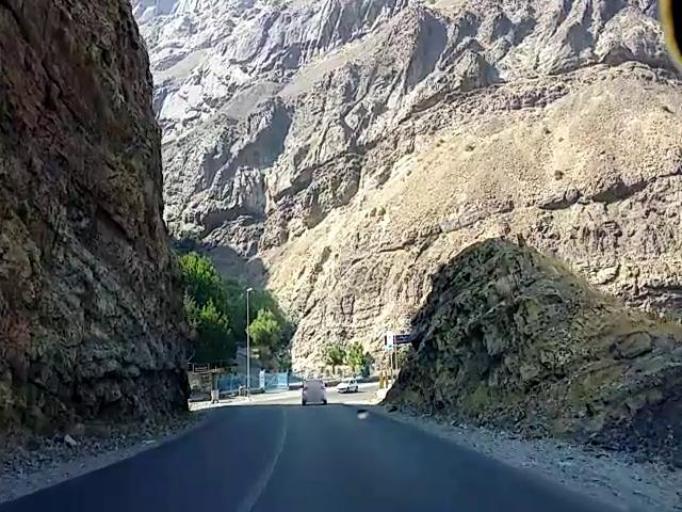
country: IR
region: Alborz
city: Karaj
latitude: 36.0031
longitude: 51.1172
